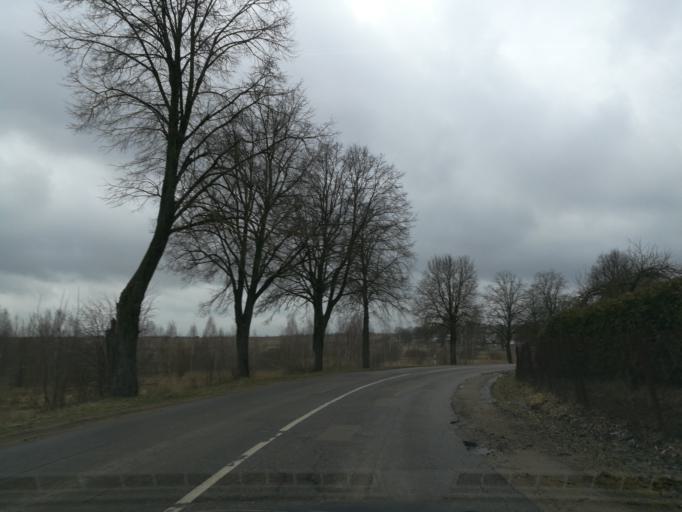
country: LT
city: Grigiskes
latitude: 54.6454
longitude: 25.0972
